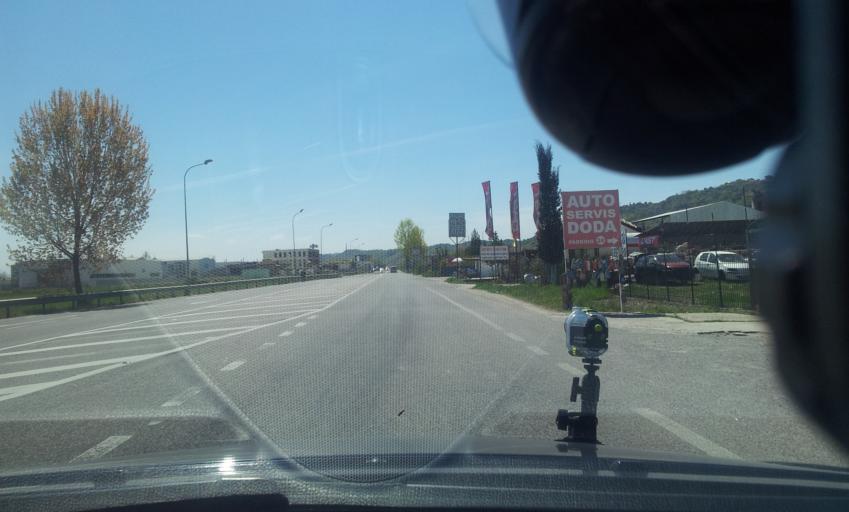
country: AL
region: Tirane
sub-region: Rrethi i Tiranes
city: Preze
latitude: 41.4349
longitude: 19.6880
